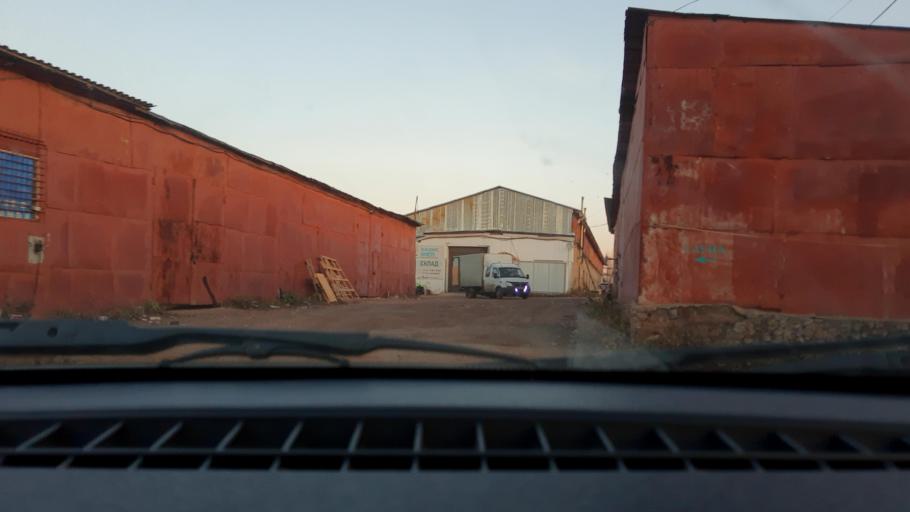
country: RU
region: Bashkortostan
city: Ufa
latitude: 54.8302
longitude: 56.0824
